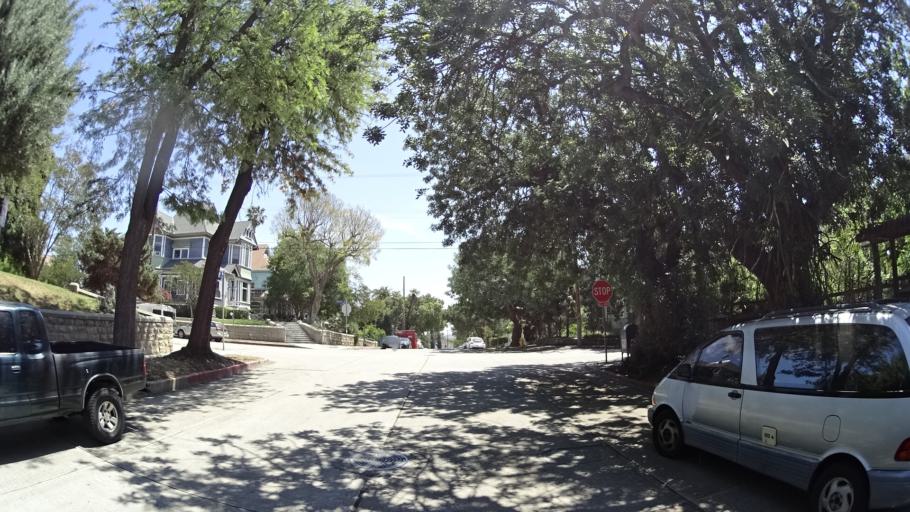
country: US
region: California
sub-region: Los Angeles County
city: Echo Park
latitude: 34.0706
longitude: -118.2548
